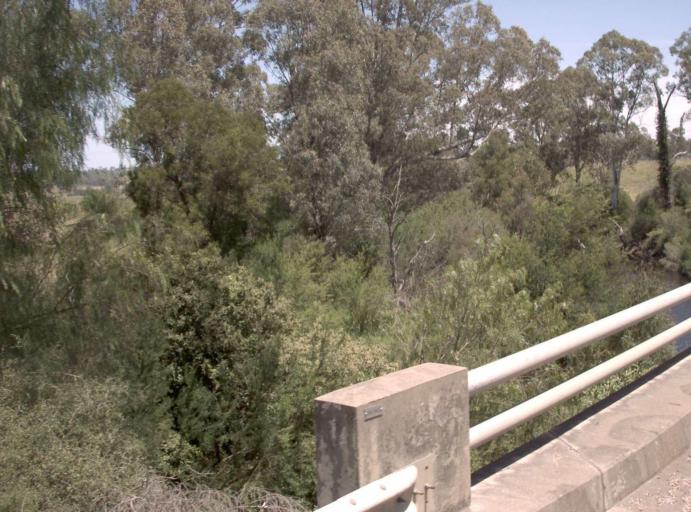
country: AU
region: Victoria
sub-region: East Gippsland
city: Bairnsdale
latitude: -37.7523
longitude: 147.7248
